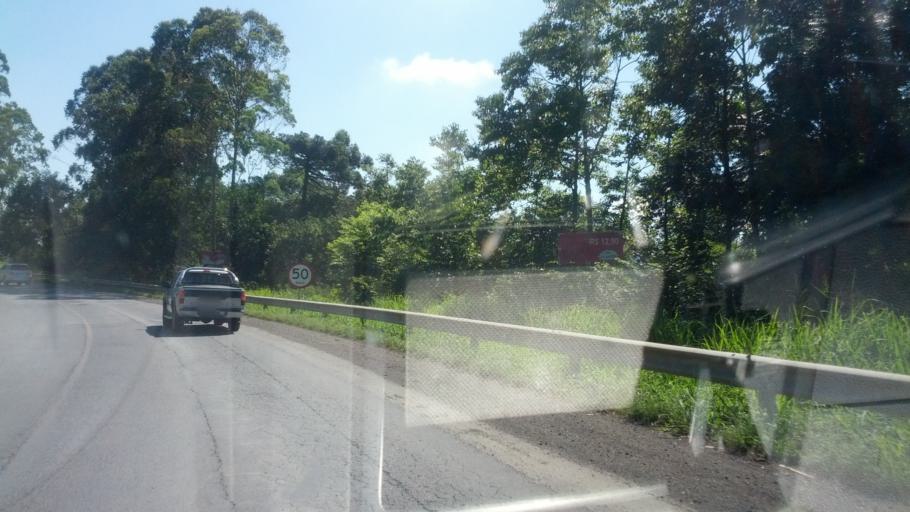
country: BR
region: Santa Catarina
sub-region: Rio Do Sul
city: Rio do Sul
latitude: -27.2152
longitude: -49.6523
